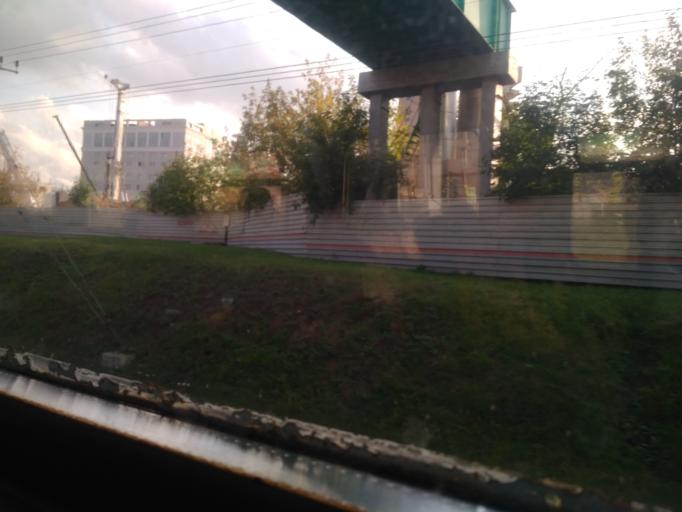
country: RU
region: Moscow
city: Lefortovo
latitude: 55.7550
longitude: 37.7176
